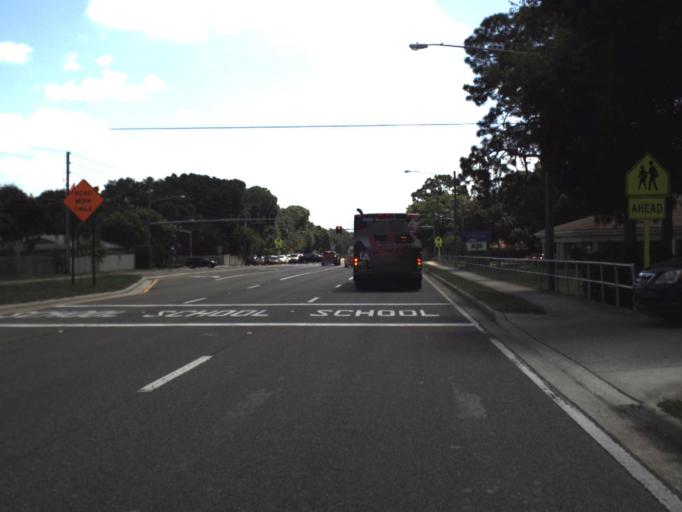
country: US
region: Florida
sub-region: Pinellas County
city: Safety Harbor
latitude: 28.0195
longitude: -82.7179
